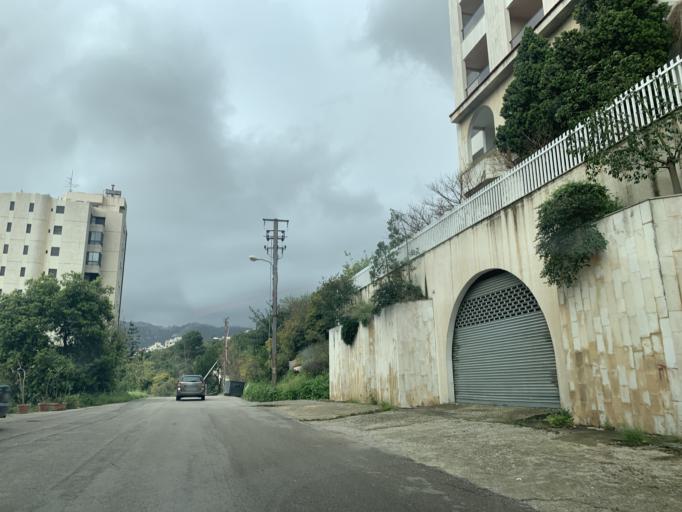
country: LB
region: Mont-Liban
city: Djounie
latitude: 34.0020
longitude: 35.6523
